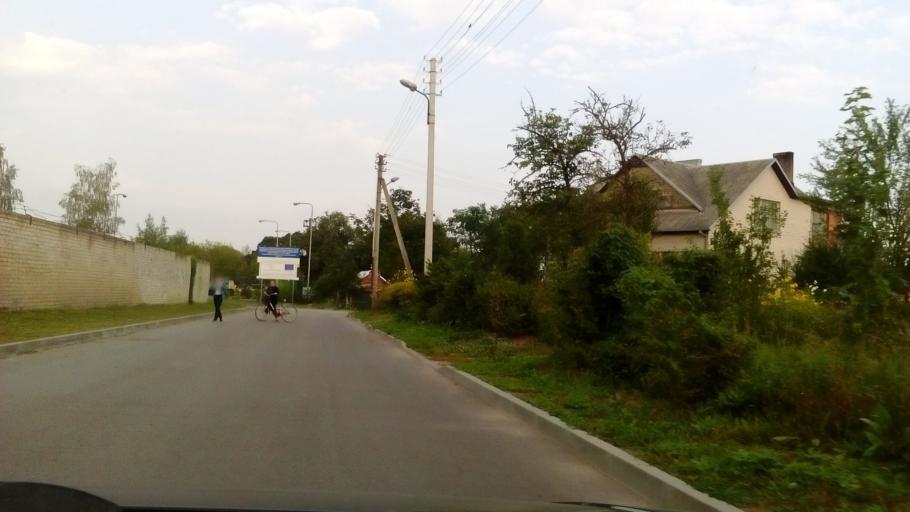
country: LT
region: Alytaus apskritis
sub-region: Alytus
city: Alytus
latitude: 54.3864
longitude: 24.0520
